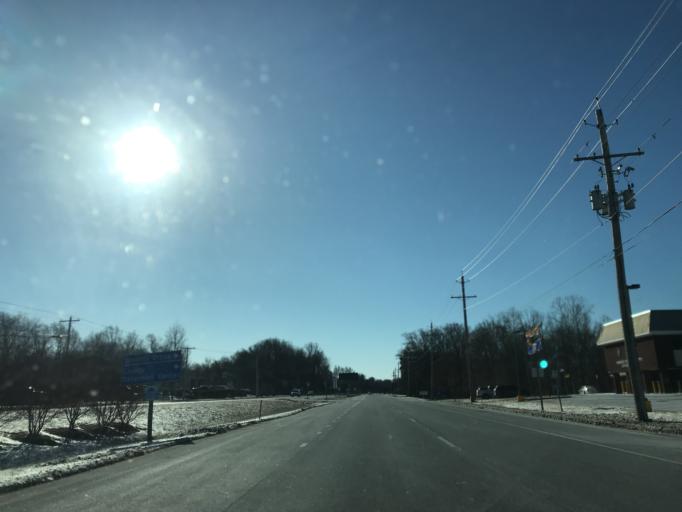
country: US
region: Maryland
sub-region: Charles County
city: La Plata
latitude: 38.5254
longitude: -76.9824
